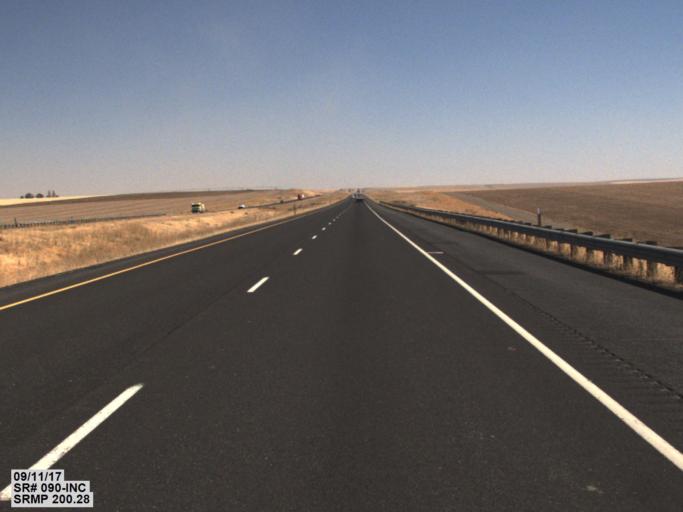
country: US
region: Washington
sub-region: Grant County
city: Warden
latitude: 47.0859
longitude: -118.8038
